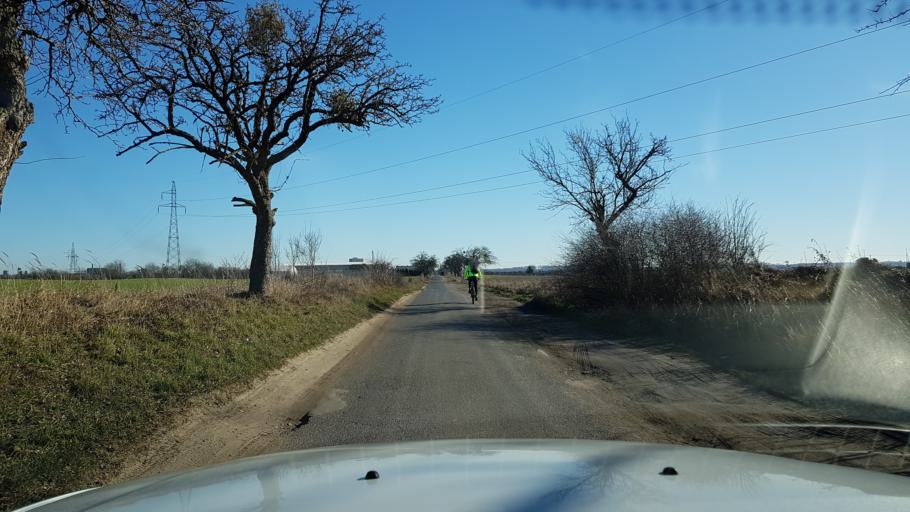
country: PL
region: West Pomeranian Voivodeship
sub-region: Powiat mysliborski
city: Barlinek
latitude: 52.9974
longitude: 15.1802
